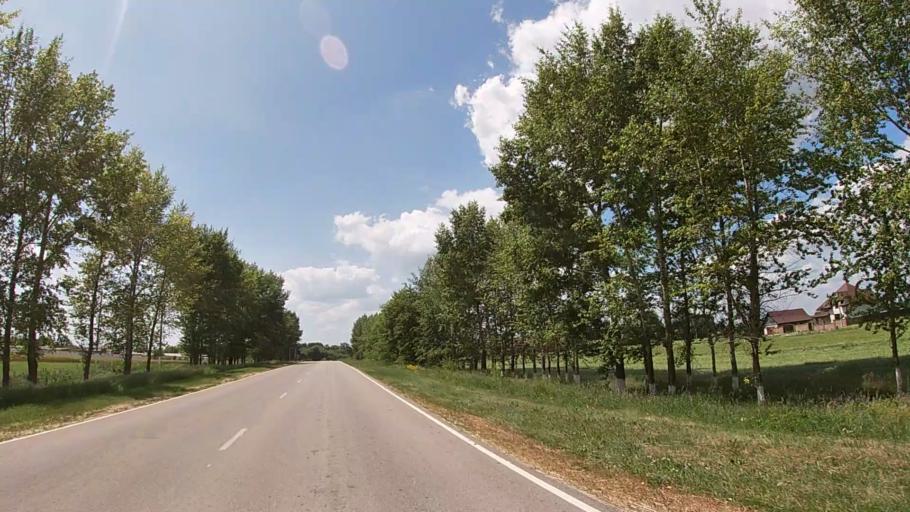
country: RU
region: Belgorod
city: Grayvoron
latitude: 50.4379
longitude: 35.6075
